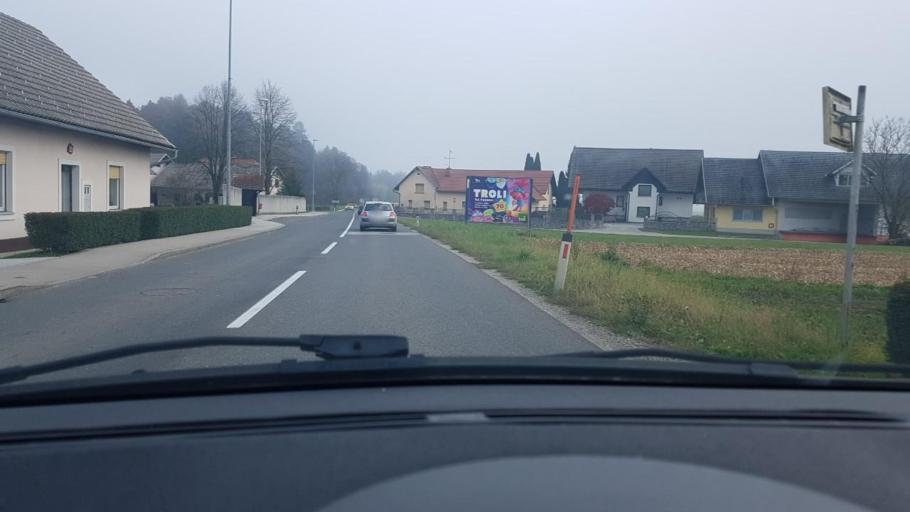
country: SI
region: Cerklje na Gorenjskem
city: Cerklje na Gorenjskem
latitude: 46.2256
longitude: 14.4904
